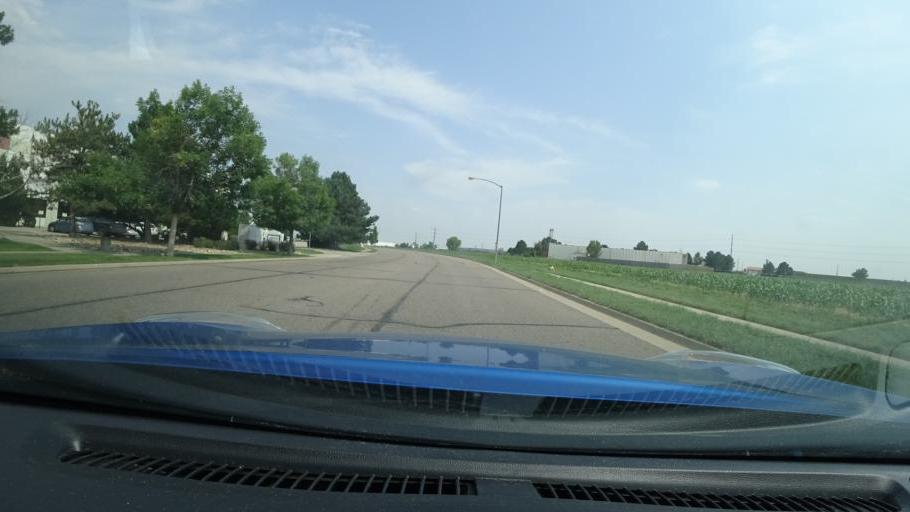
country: US
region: Colorado
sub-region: Adams County
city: Aurora
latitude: 39.7575
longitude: -104.7417
